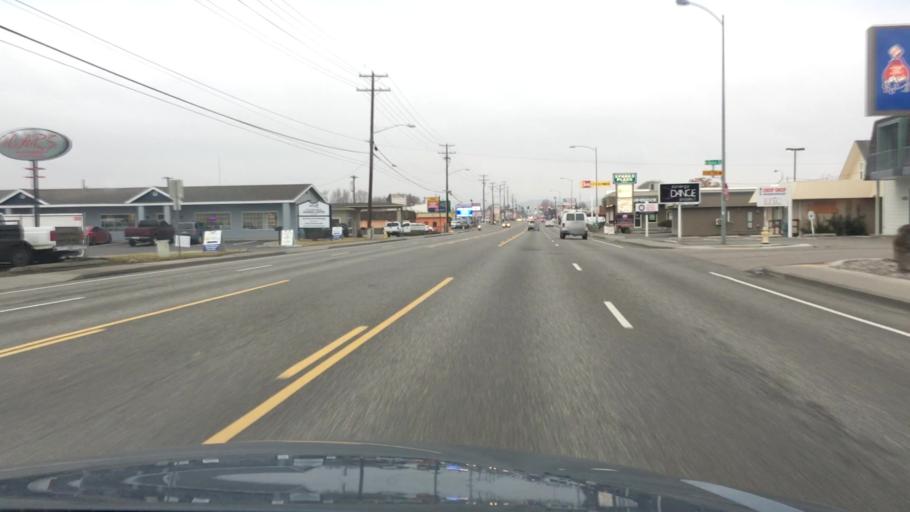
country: US
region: Washington
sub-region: Franklin County
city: West Pasco
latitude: 46.2124
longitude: -119.1741
